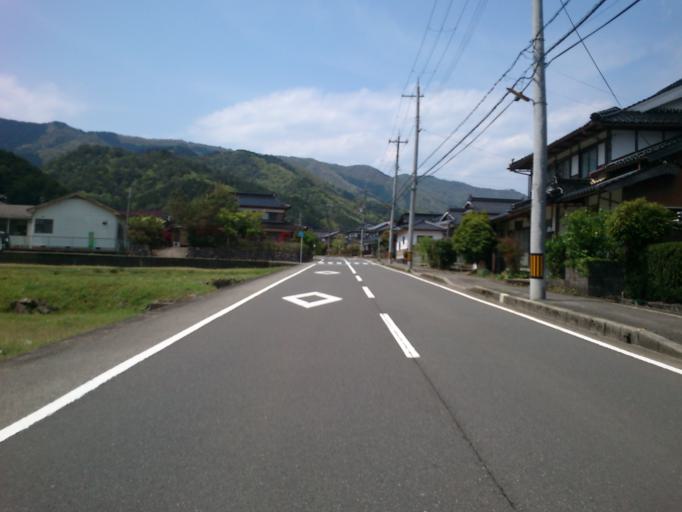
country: JP
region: Kyoto
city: Fukuchiyama
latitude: 35.3531
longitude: 134.9436
